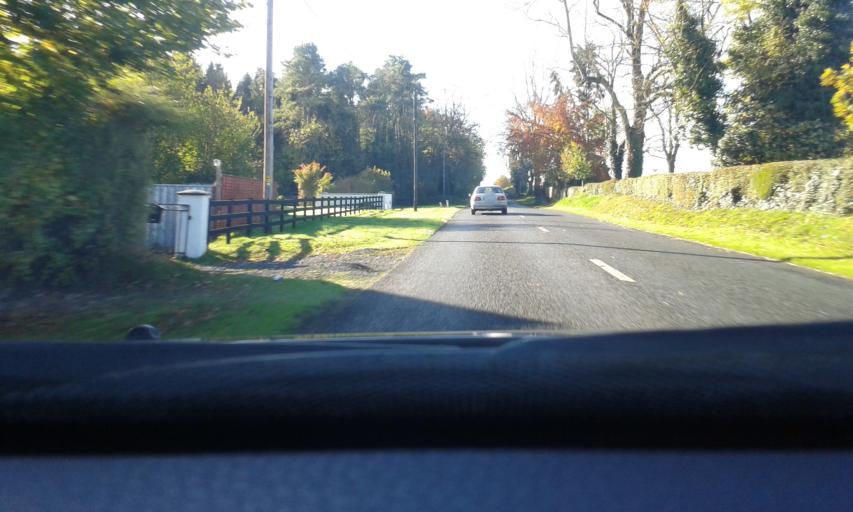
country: IE
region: Leinster
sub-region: Kildare
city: Rathangan
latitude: 53.1910
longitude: -7.0112
